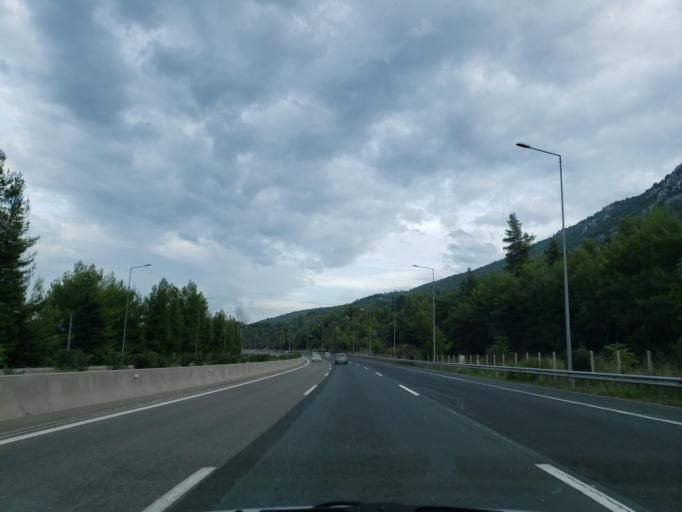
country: GR
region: Attica
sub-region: Nomarchia Anatolikis Attikis
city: Afidnes
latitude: 38.2297
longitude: 23.8044
